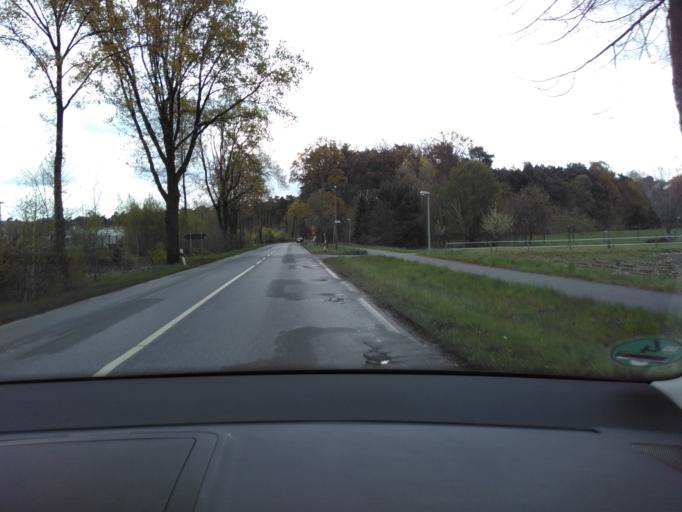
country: DE
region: North Rhine-Westphalia
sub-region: Regierungsbezirk Detmold
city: Verl
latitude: 51.8844
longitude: 8.4568
